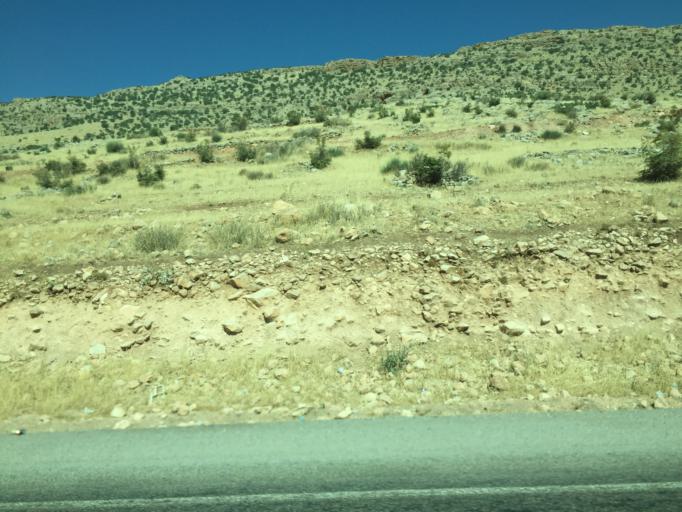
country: TR
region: Batman
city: Hasankeyf
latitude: 37.6899
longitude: 41.4558
